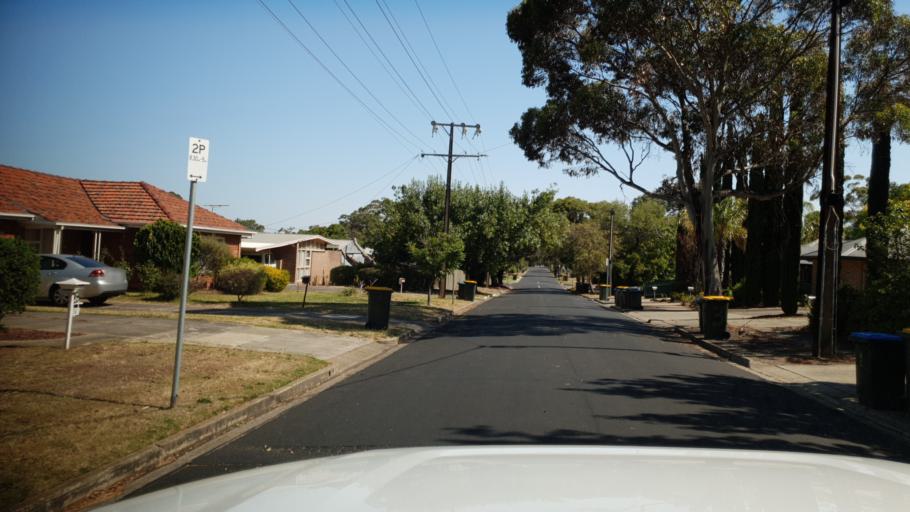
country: AU
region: South Australia
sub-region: Mitcham
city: Clapham
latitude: -34.9951
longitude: 138.5877
